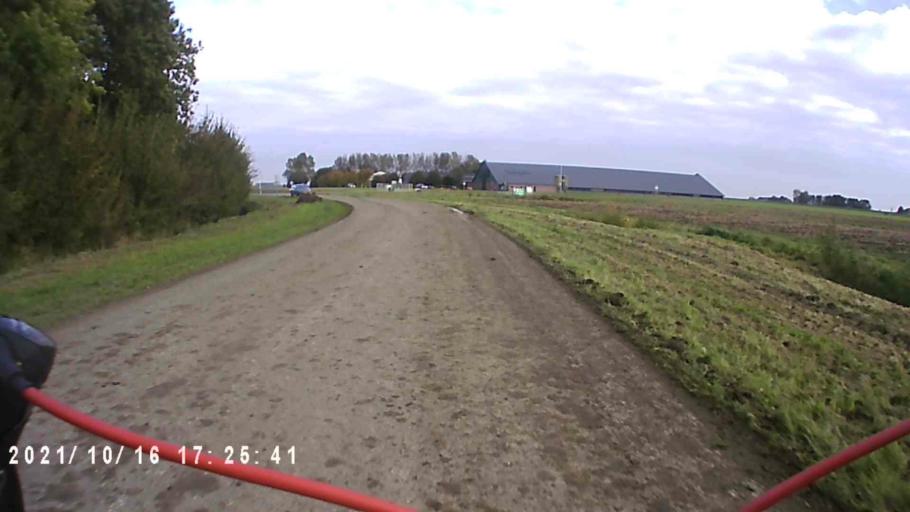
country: NL
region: Friesland
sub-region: Gemeente Kollumerland en Nieuwkruisland
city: Kollum
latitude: 53.3208
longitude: 6.1903
